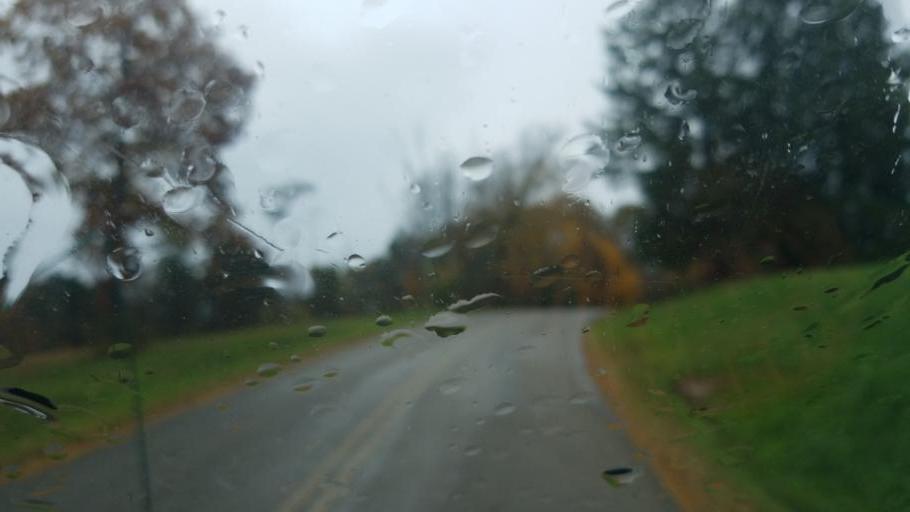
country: US
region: West Virginia
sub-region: Wood County
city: Blennerhassett
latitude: 39.3427
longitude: -81.6286
